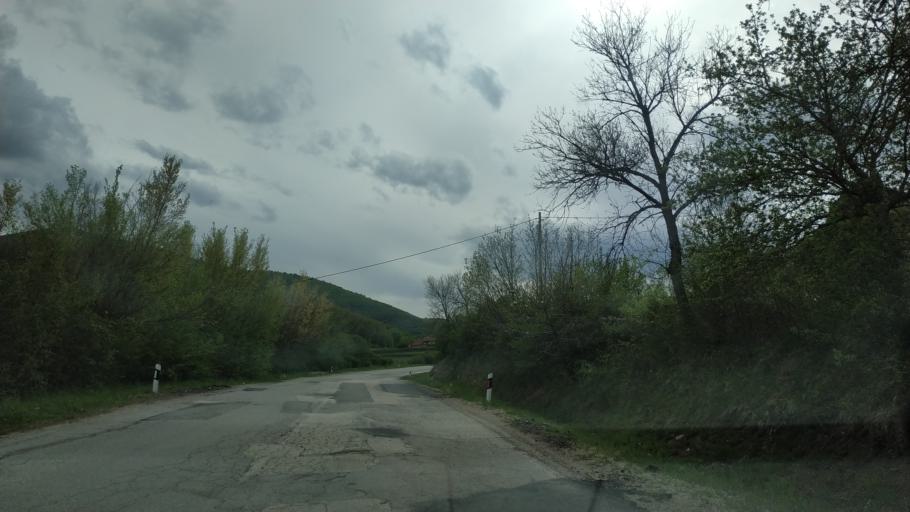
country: RS
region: Central Serbia
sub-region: Zajecarski Okrug
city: Soko Banja
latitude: 43.6439
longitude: 21.8945
